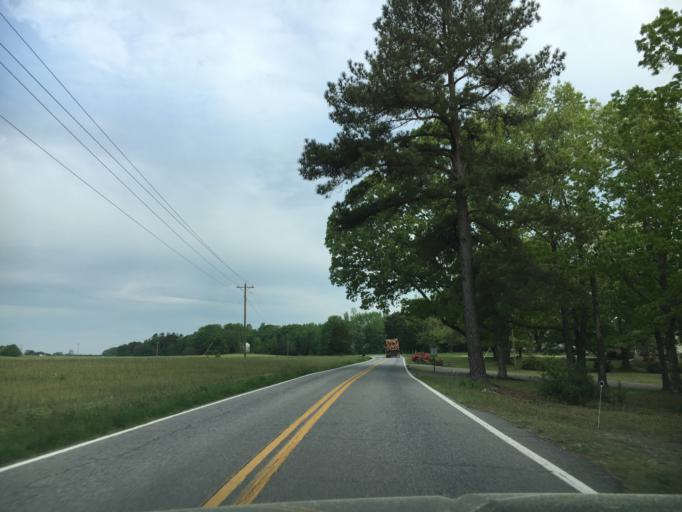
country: US
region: Virginia
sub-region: Halifax County
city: Halifax
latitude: 36.8968
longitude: -78.8549
